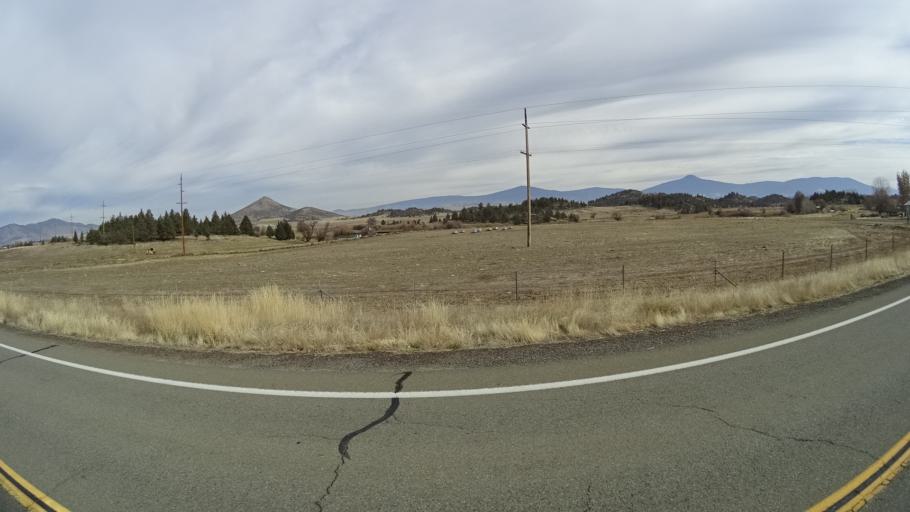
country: US
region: California
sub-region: Siskiyou County
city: Montague
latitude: 41.6845
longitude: -122.5342
